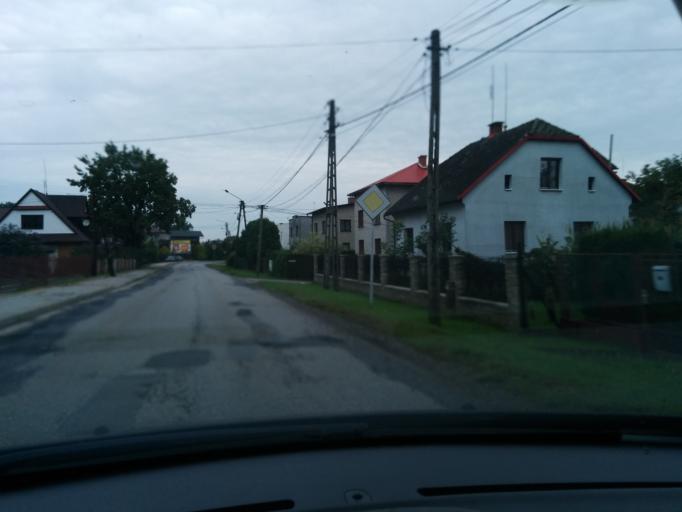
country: PL
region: Silesian Voivodeship
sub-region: Powiat bielski
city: Bujakow
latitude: 49.8720
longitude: 19.1961
